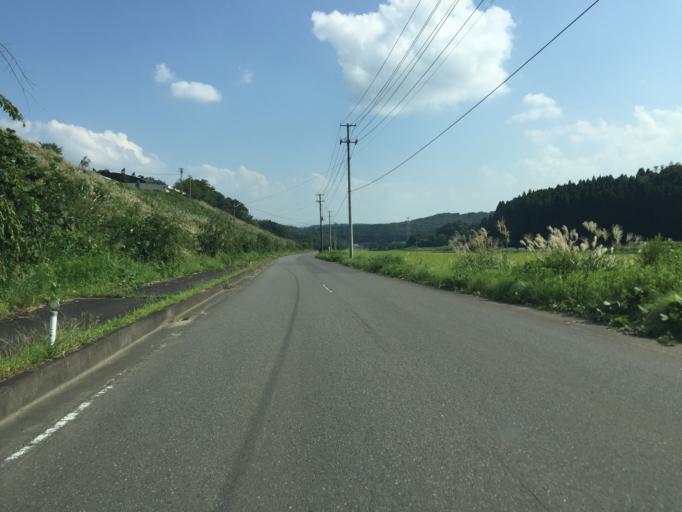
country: JP
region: Fukushima
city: Nihommatsu
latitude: 37.6063
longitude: 140.3963
